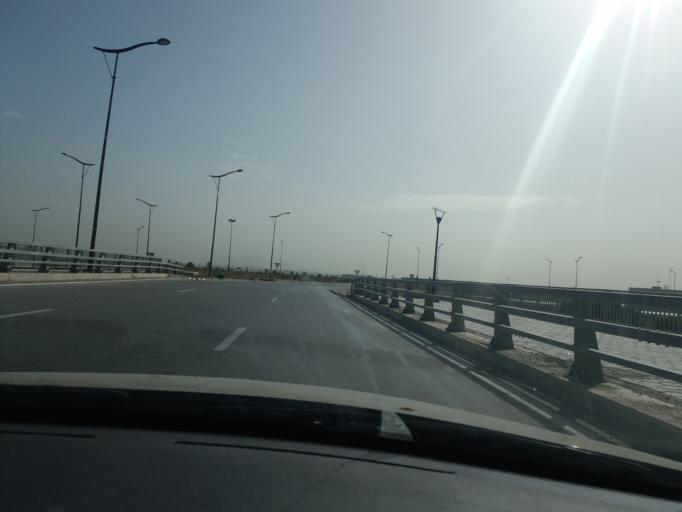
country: TN
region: Tunis
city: Tunis
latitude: 36.8047
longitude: 10.1964
